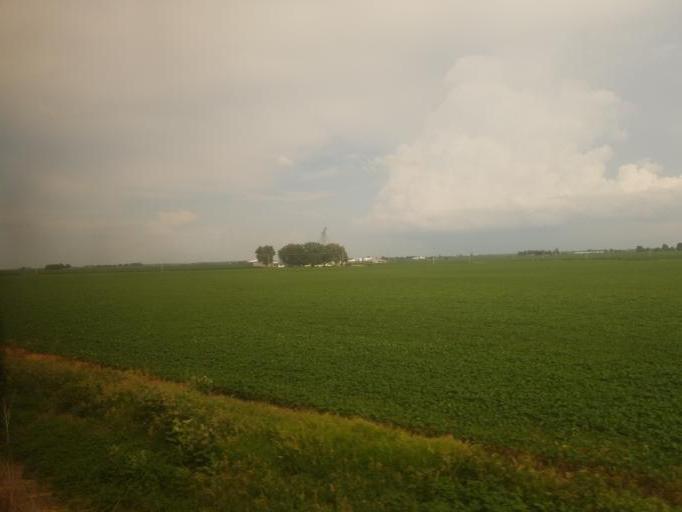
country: US
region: Illinois
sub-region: Henry County
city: Galva
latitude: 41.1236
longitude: -90.1394
